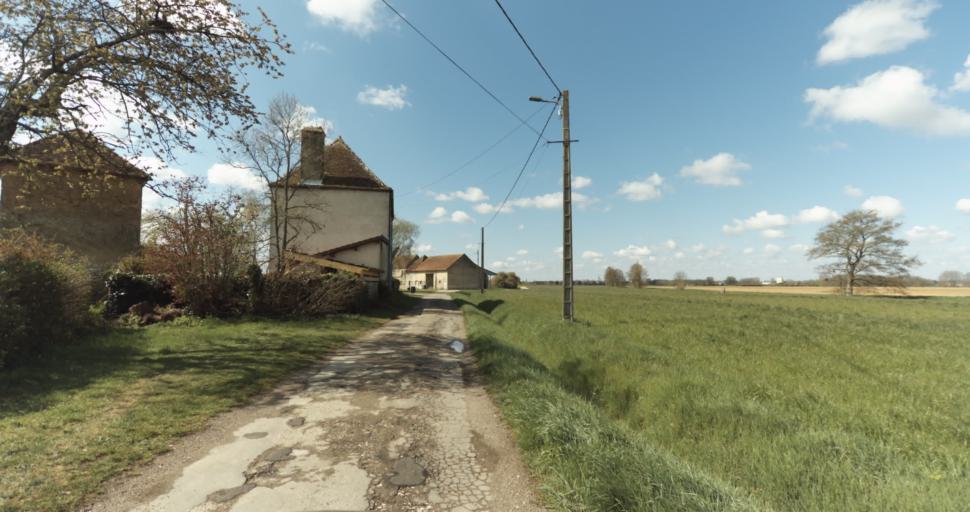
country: FR
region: Bourgogne
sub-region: Departement de la Cote-d'Or
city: Auxonne
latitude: 47.2025
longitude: 5.4235
